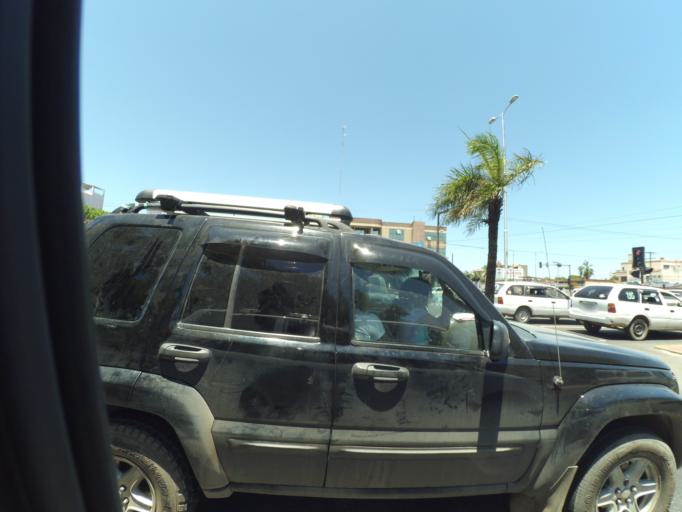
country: BO
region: Santa Cruz
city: Santa Cruz de la Sierra
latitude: -17.7990
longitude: -63.1924
